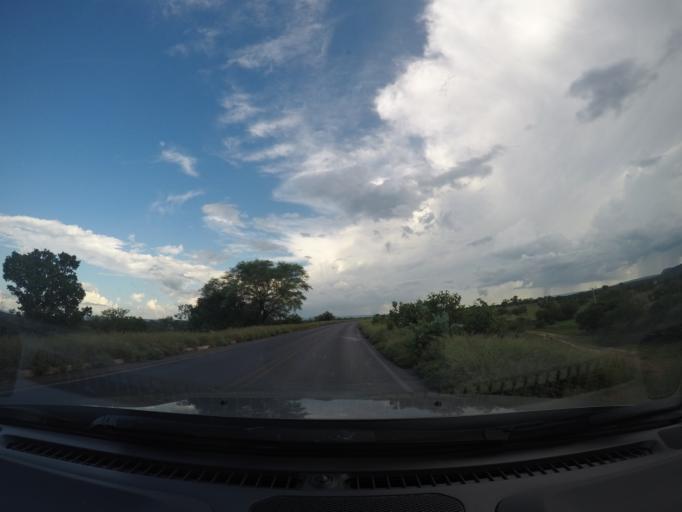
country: BR
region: Bahia
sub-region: Ibotirama
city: Ibotirama
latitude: -12.1443
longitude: -43.3160
